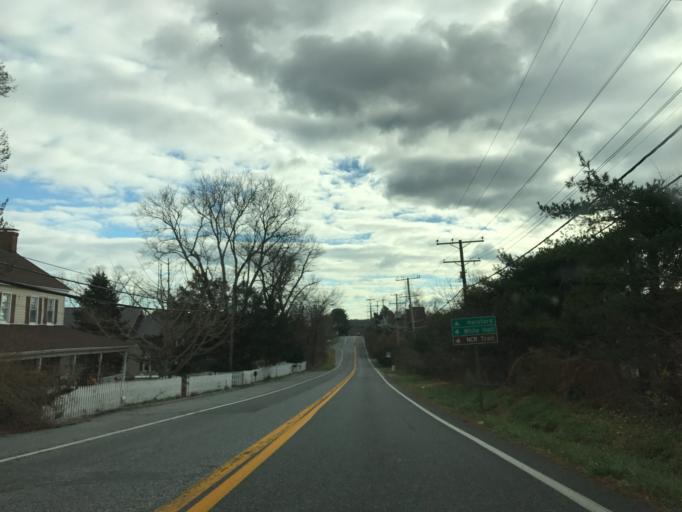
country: US
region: Pennsylvania
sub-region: York County
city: New Freedom
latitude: 39.6248
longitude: -76.6588
